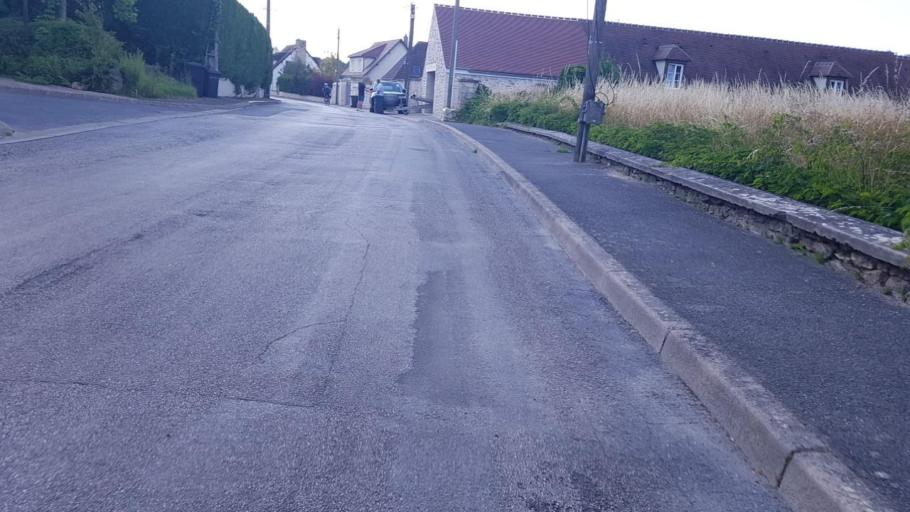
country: FR
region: Picardie
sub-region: Departement de l'Oise
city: Senlis
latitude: 49.1990
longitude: 2.5950
